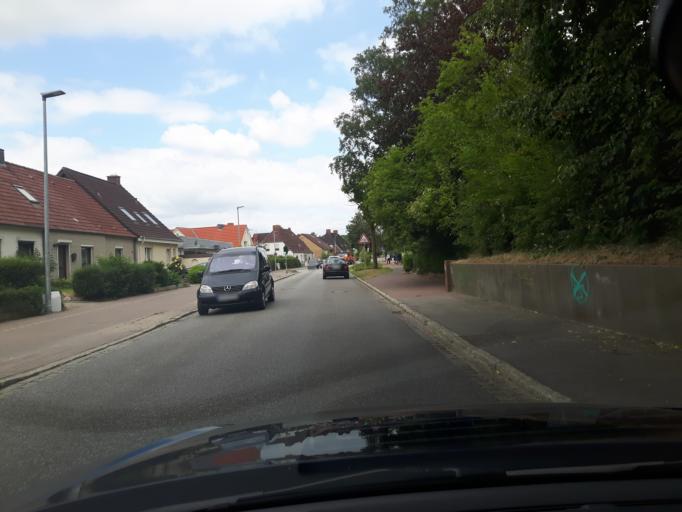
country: DE
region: Schleswig-Holstein
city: Neustadt in Holstein
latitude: 54.0983
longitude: 10.8219
